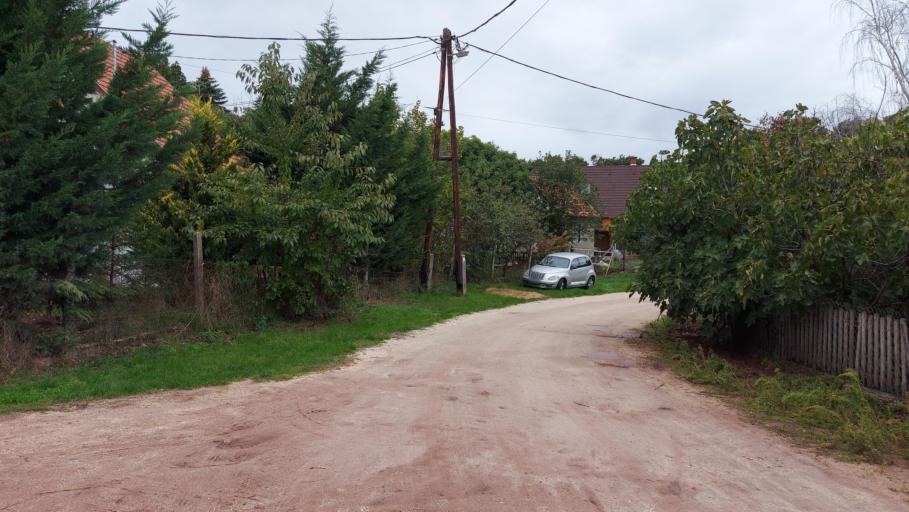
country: HU
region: Veszprem
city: Balatonalmadi
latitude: 47.0294
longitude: 17.9975
